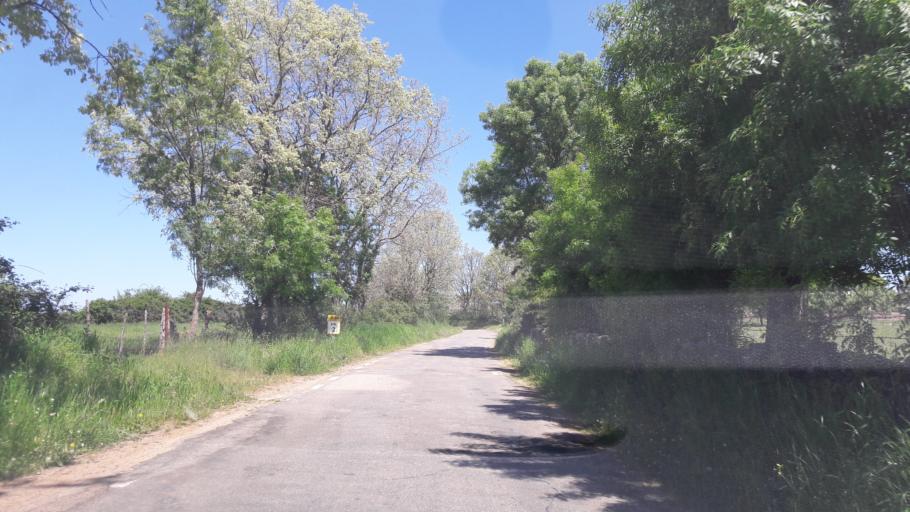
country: ES
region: Castille and Leon
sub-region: Provincia de Salamanca
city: Endrinal
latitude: 40.5762
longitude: -5.8061
